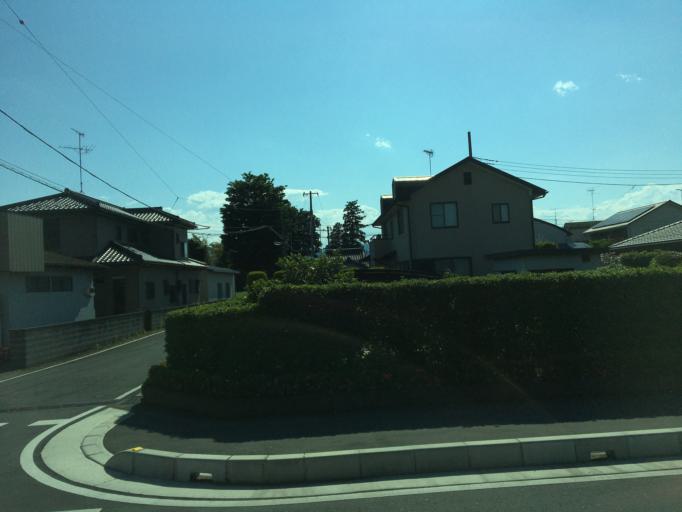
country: JP
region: Saitama
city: Sakado
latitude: 35.9689
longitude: 139.3425
